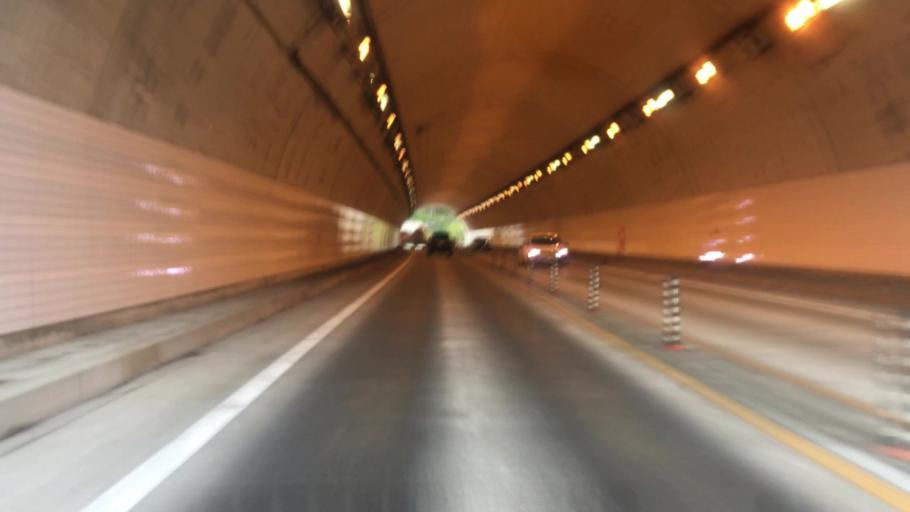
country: JP
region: Kyoto
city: Fukuchiyama
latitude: 35.2728
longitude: 134.9948
